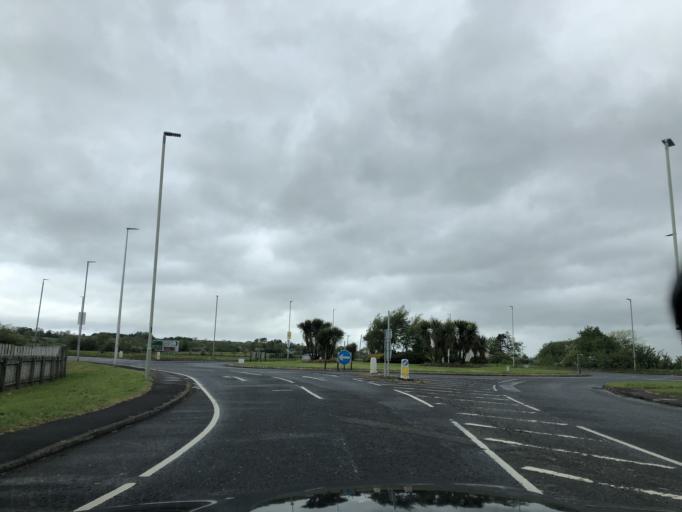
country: GB
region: Northern Ireland
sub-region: Ballymoney District
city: Ballymoney
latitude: 55.0808
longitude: -6.5251
